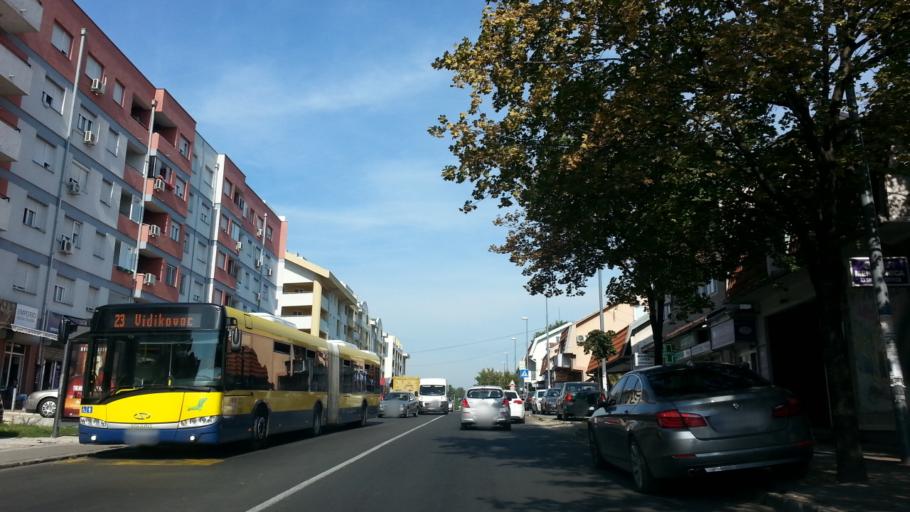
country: RS
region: Central Serbia
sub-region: Belgrade
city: Rakovica
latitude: 44.7482
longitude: 20.4309
